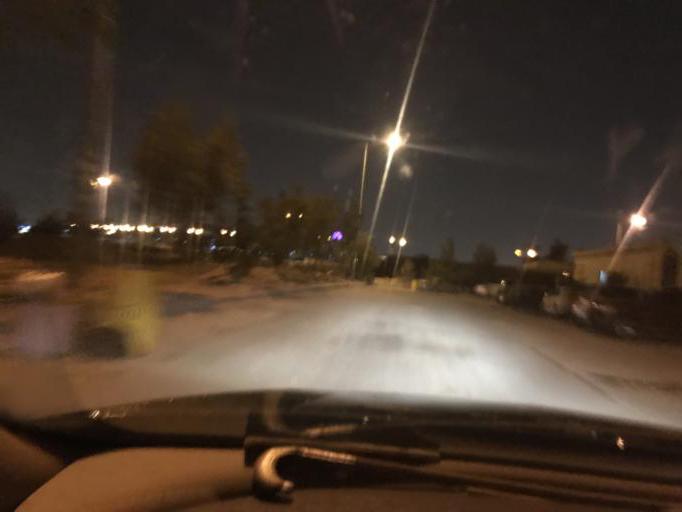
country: SA
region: Ar Riyad
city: Riyadh
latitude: 24.8181
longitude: 46.7204
